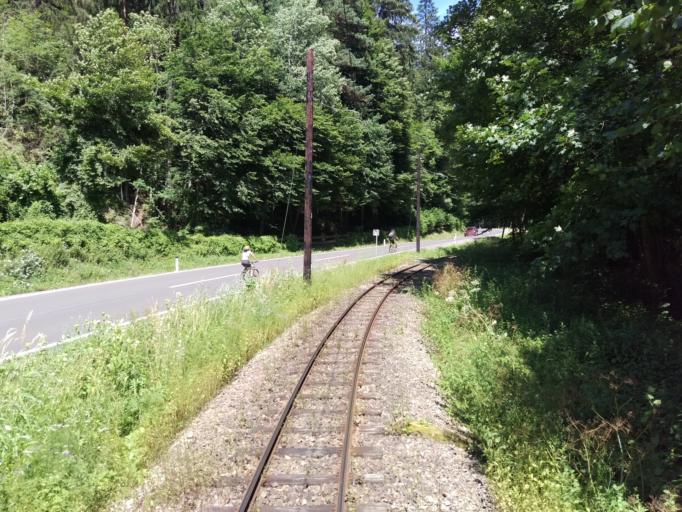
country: AT
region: Styria
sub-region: Politischer Bezirk Bruck-Muerzzuschlag
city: Pernegg an der Mur
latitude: 47.3636
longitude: 15.3775
